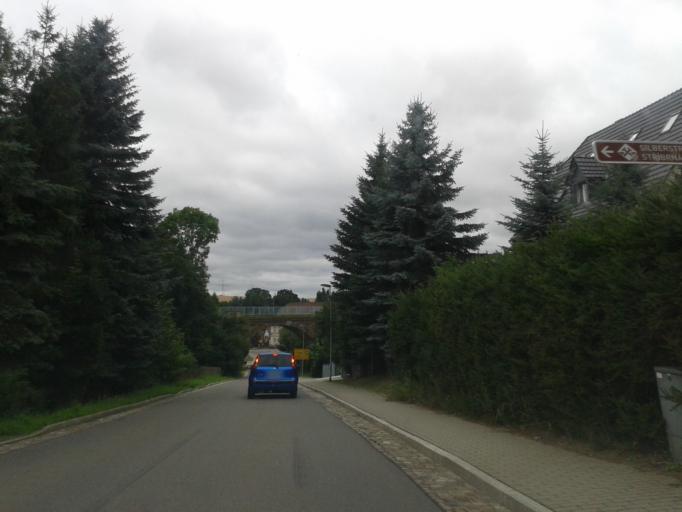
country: DE
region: Saxony
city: Niederschona
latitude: 50.9382
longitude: 13.4198
